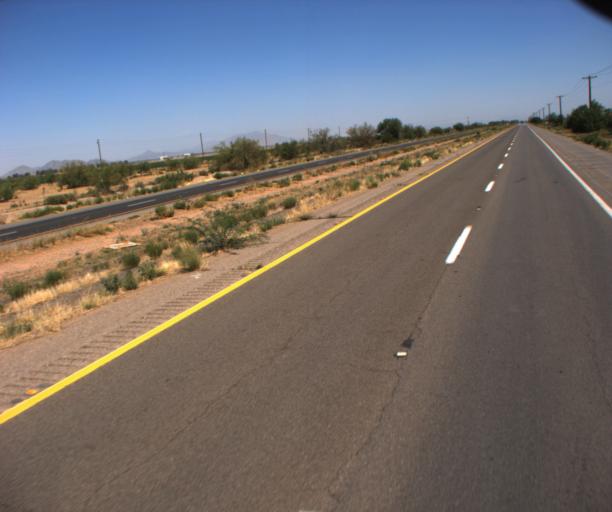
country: US
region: Arizona
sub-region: Pinal County
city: Maricopa
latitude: 32.9094
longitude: -112.0493
